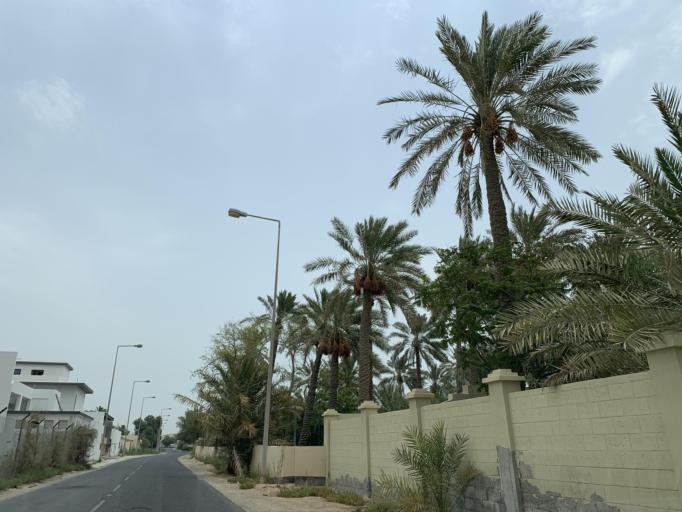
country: BH
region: Northern
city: Madinat `Isa
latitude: 26.1867
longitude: 50.4674
